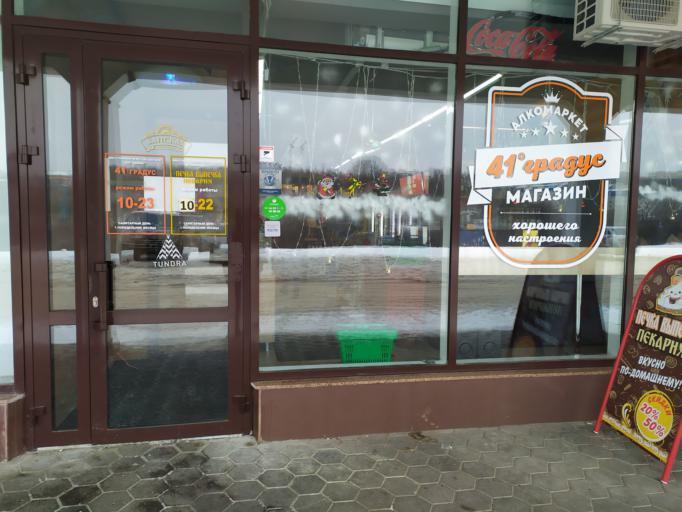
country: RU
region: Chuvashia
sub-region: Cheboksarskiy Rayon
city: Cheboksary
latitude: 56.1194
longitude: 47.2081
